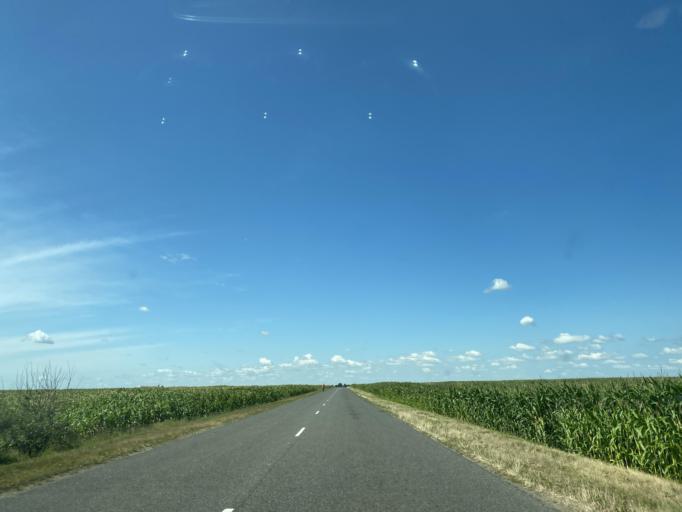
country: BY
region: Brest
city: Ivanava
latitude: 52.1757
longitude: 25.5846
